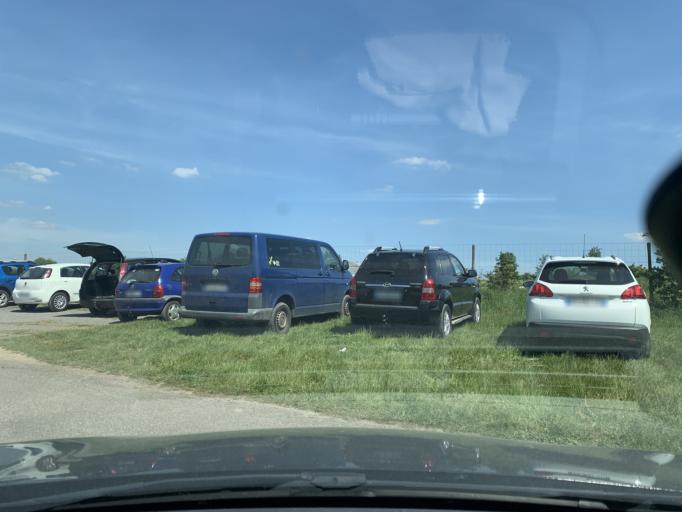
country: FR
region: Nord-Pas-de-Calais
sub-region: Departement du Nord
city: Caudry
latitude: 50.1005
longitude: 3.4206
